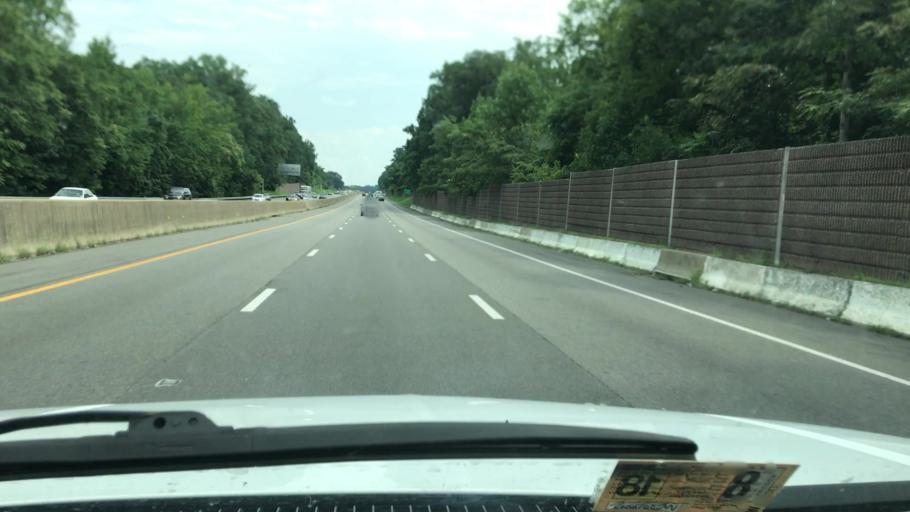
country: US
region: Virginia
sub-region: Chesterfield County
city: Bon Air
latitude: 37.4897
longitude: -77.5201
